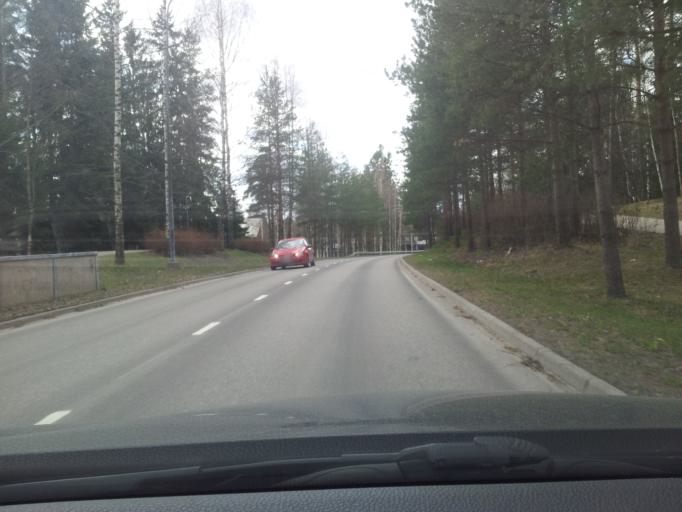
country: FI
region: Uusimaa
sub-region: Helsinki
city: Koukkuniemi
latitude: 60.1720
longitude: 24.7382
